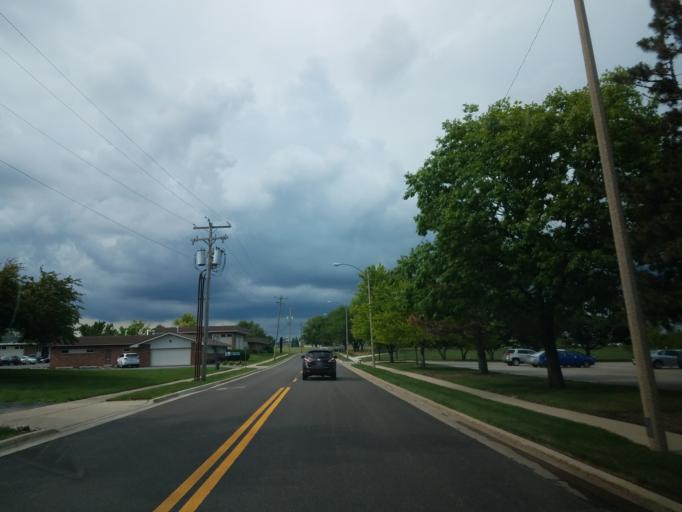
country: US
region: Illinois
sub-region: McLean County
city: Bloomington
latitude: 40.4785
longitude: -88.9572
